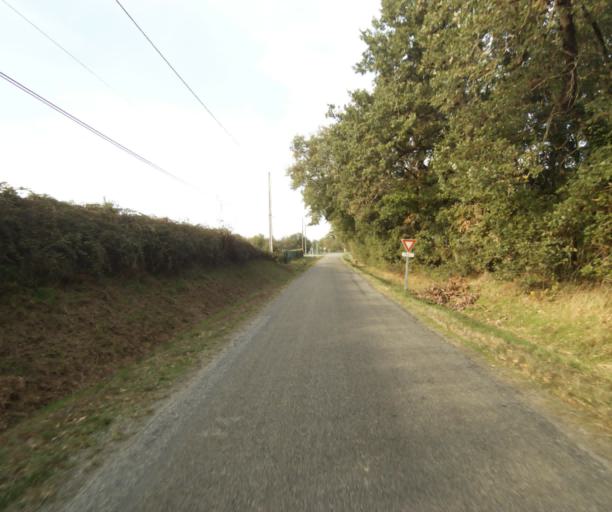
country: FR
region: Midi-Pyrenees
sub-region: Departement du Tarn-et-Garonne
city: Campsas
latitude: 43.8813
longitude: 1.3234
